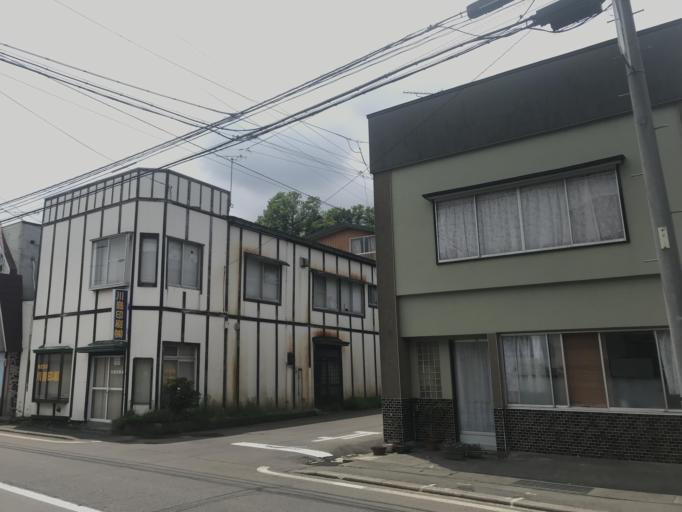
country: JP
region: Aomori
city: Shimokizukuri
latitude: 40.7795
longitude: 140.2078
